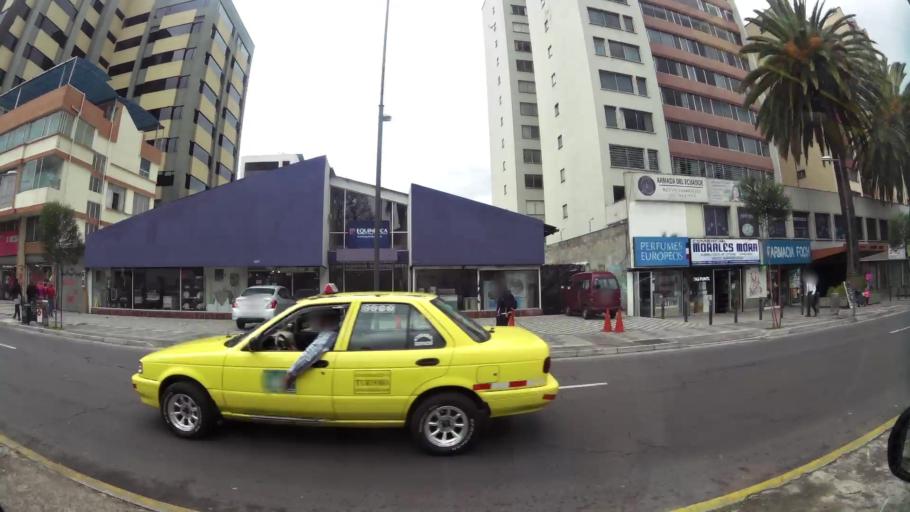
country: EC
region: Pichincha
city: Quito
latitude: -0.1995
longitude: -78.4927
